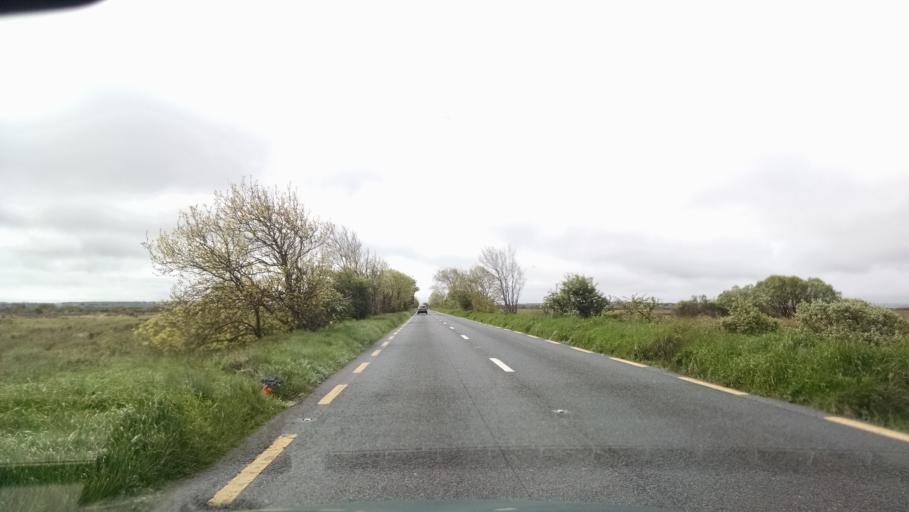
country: IE
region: Connaught
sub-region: County Galway
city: Claregalway
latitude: 53.3574
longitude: -9.0178
